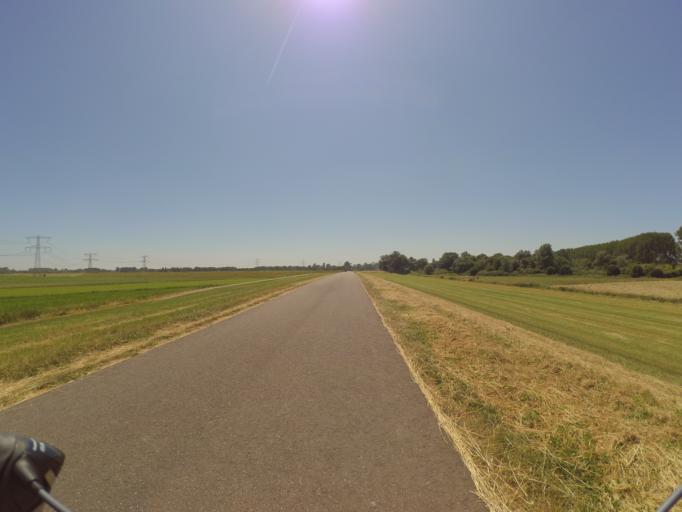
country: NL
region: South Holland
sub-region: Gemeente Sliedrecht
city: Sliedrecht
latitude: 51.7993
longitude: 4.7395
